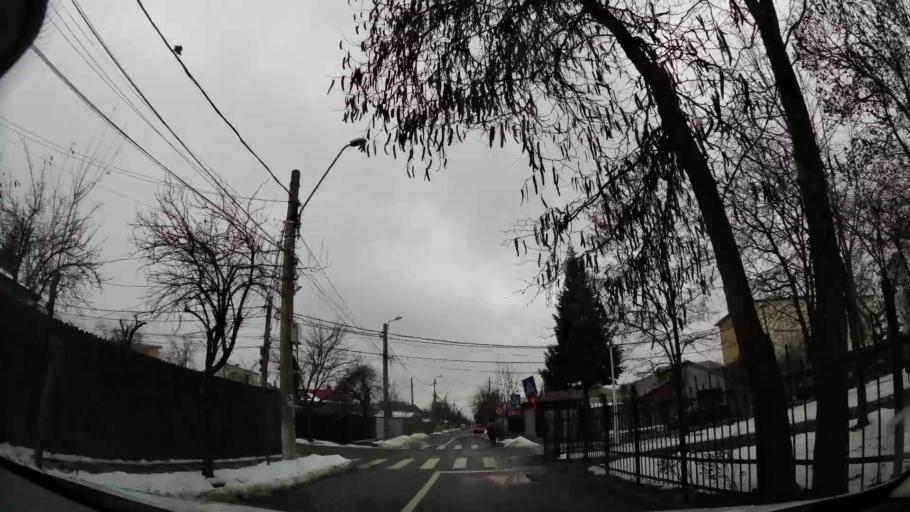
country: RO
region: Ilfov
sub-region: Comuna Chiajna
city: Rosu
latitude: 44.4868
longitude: 26.0168
